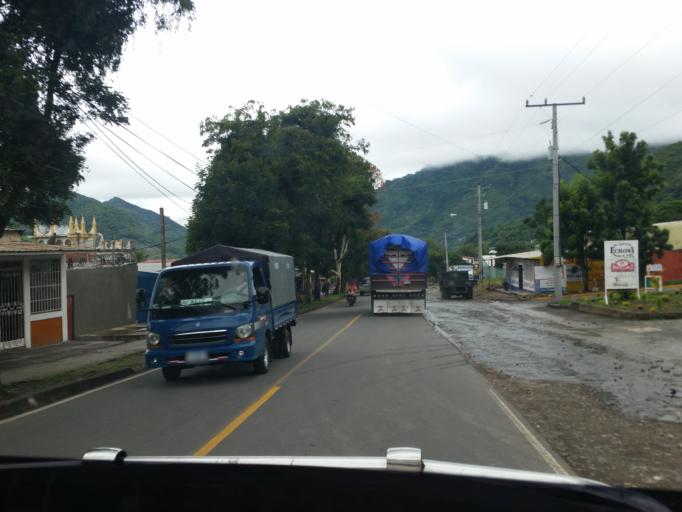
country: NI
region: Jinotega
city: Jinotega
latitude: 13.0884
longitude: -85.9945
